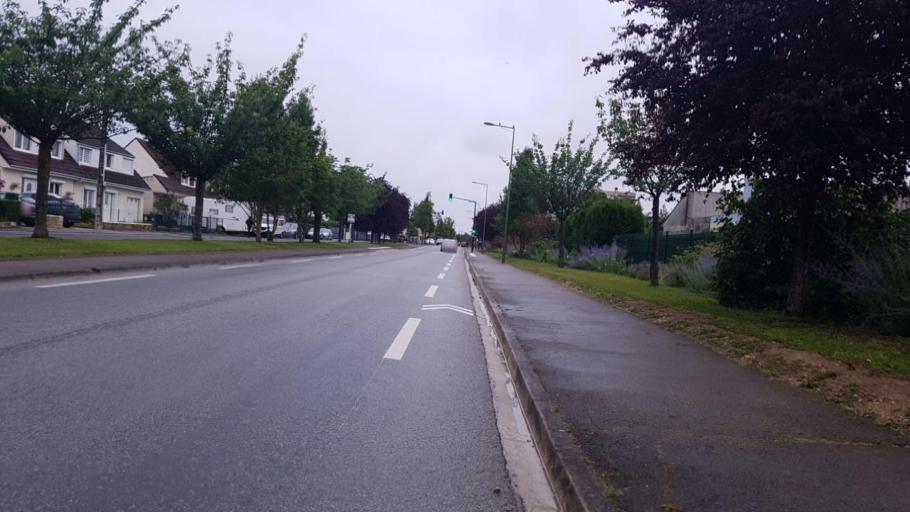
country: FR
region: Champagne-Ardenne
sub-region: Departement de la Marne
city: Saint-Memmie
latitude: 48.9357
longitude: 4.3867
